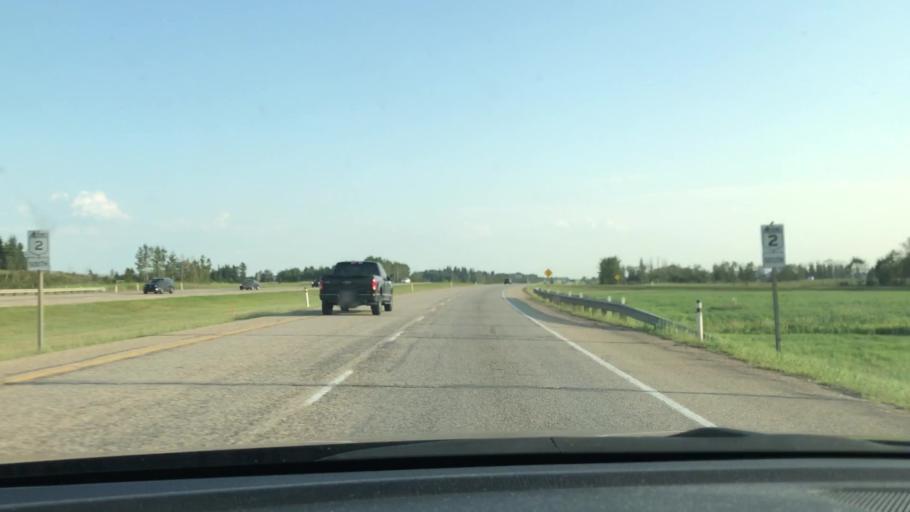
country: CA
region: Alberta
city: Lacombe
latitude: 52.5555
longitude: -113.6631
